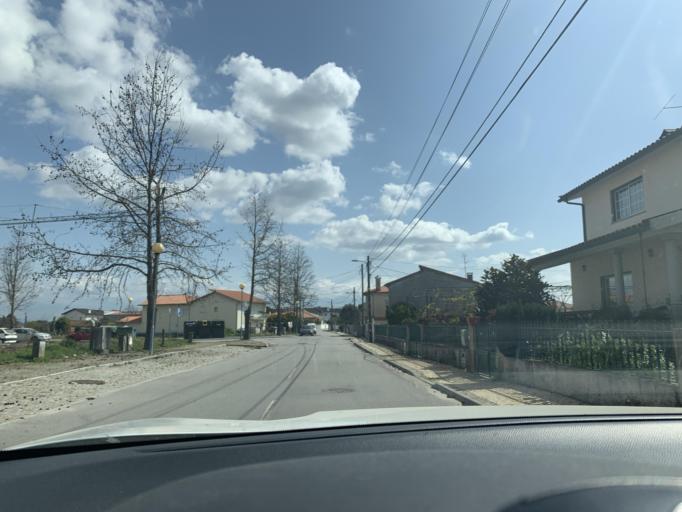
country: PT
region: Viseu
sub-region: Viseu
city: Rio de Loba
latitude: 40.6392
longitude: -7.8622
